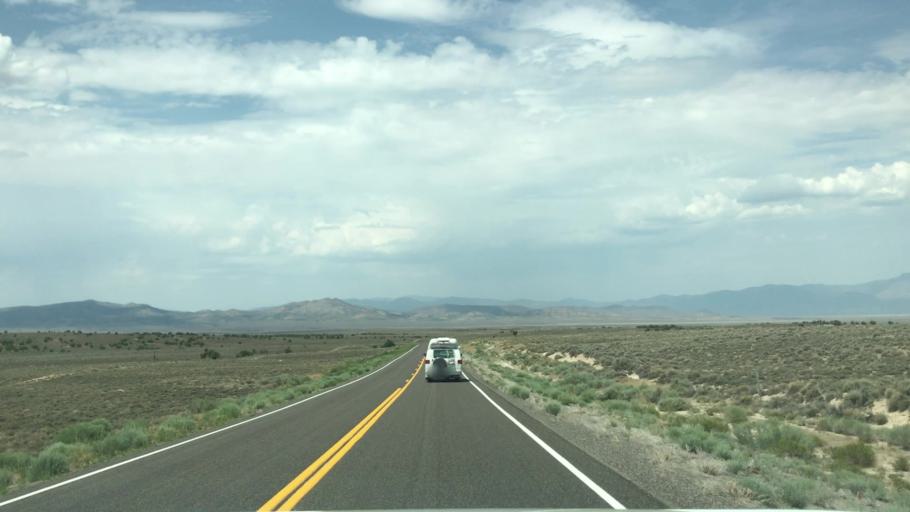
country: US
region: Nevada
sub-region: Eureka County
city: Eureka
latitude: 39.3947
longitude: -115.5286
